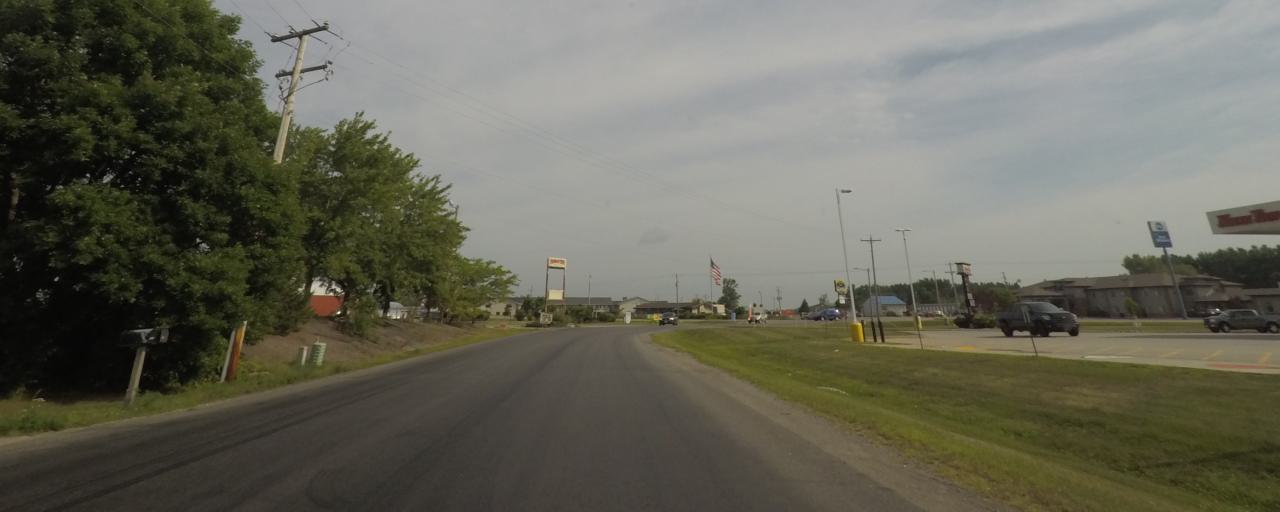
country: US
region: Wisconsin
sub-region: Portage County
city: Plover
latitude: 44.4274
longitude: -89.5160
